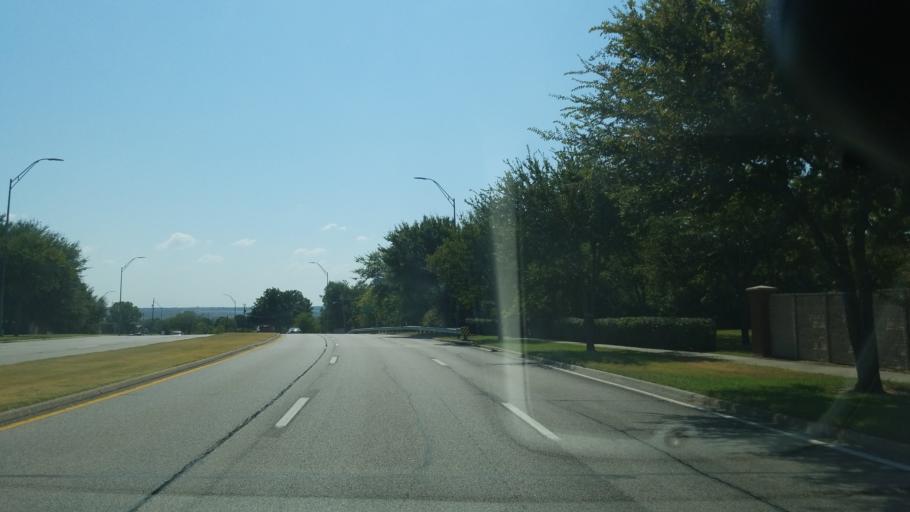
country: US
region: Texas
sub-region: Dallas County
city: Grand Prairie
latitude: 32.7064
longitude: -96.9885
